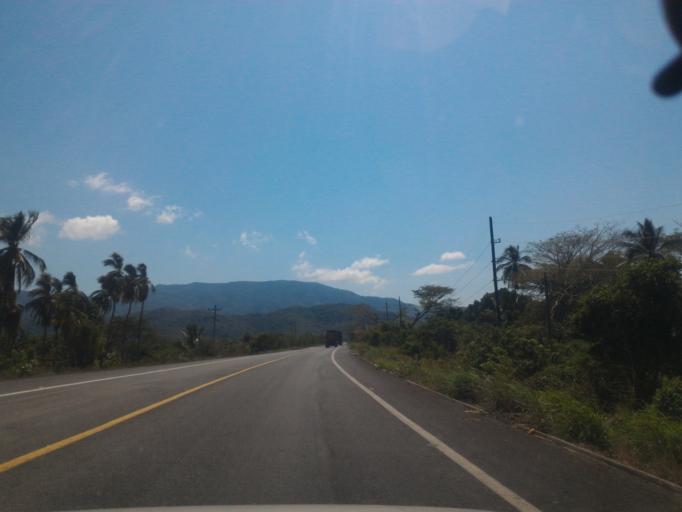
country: MX
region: Michoacan
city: Coahuayana Viejo
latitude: 18.6705
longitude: -103.6730
